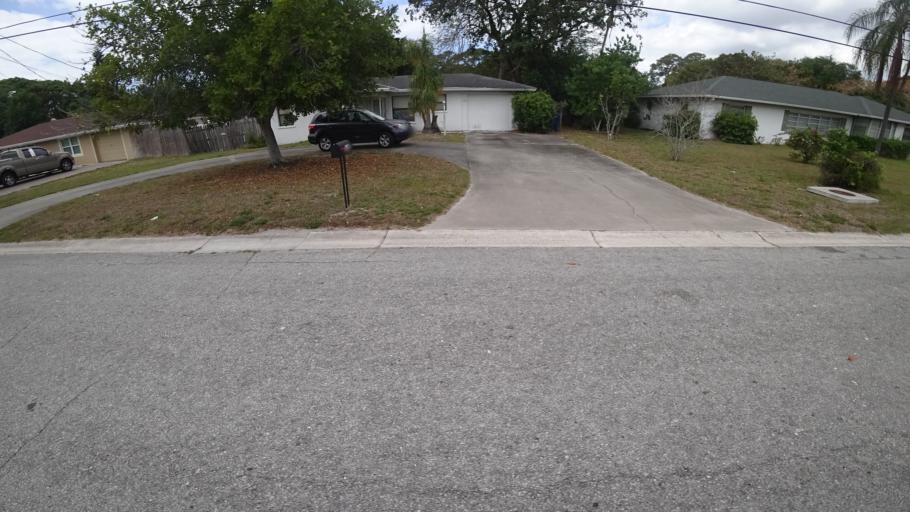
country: US
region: Florida
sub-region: Manatee County
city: South Bradenton
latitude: 27.4468
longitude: -82.5787
